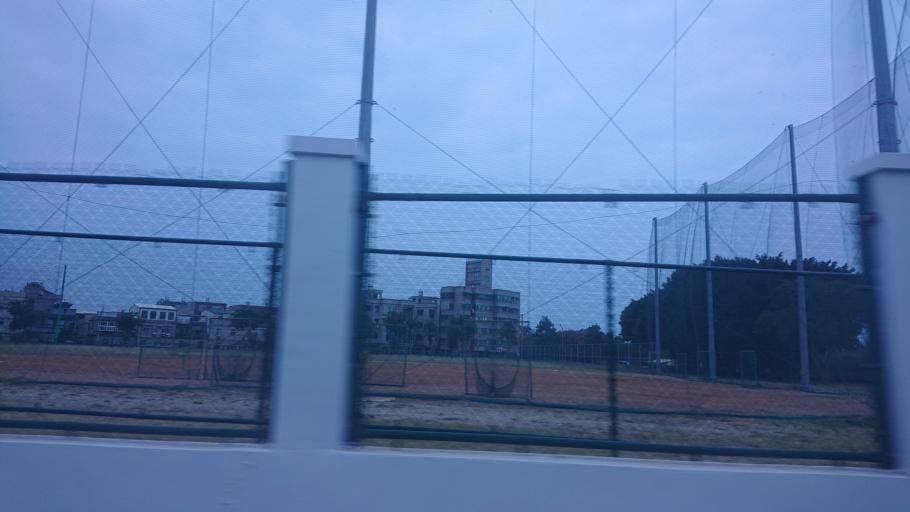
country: TW
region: Fukien
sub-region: Kinmen
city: Jincheng
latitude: 24.4354
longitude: 118.3132
